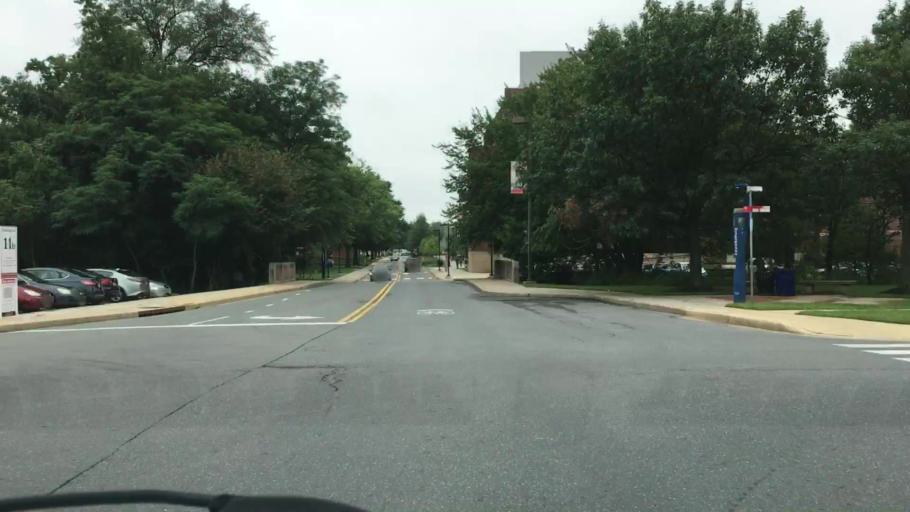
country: US
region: Maryland
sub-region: Prince George's County
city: College Park
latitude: 38.9938
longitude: -76.9373
